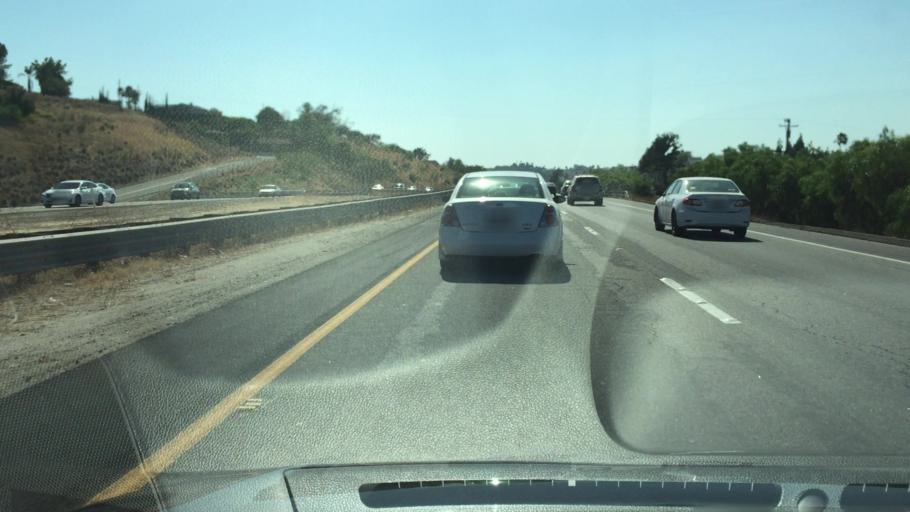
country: US
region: California
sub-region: San Diego County
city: Spring Valley
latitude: 32.7447
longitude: -116.9807
